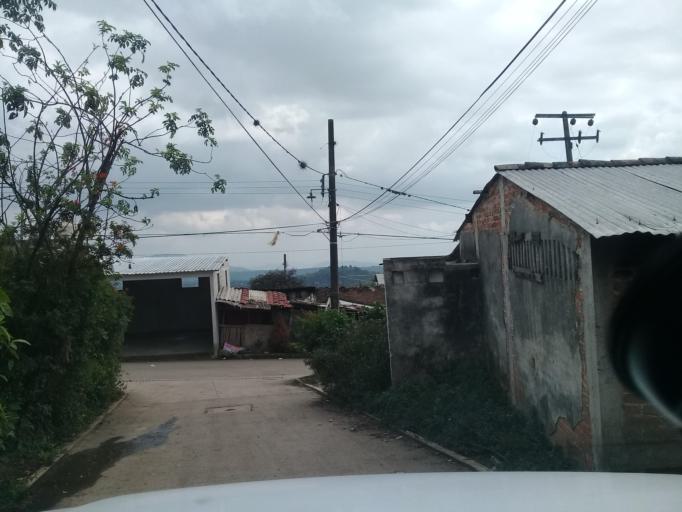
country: MX
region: Veracruz
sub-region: Xalapa
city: Fraccionamiento las Fuentes
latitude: 19.4787
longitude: -96.8797
